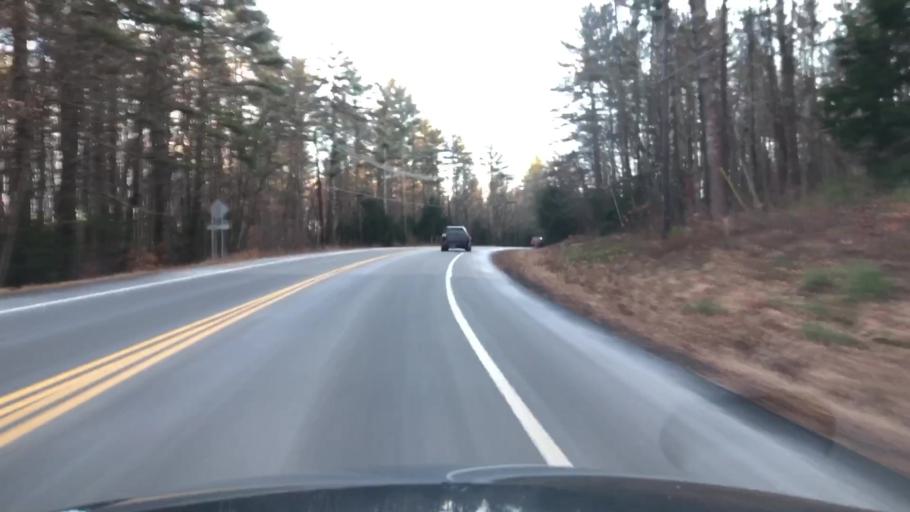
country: US
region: New Hampshire
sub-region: Hillsborough County
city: Brookline
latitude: 42.7473
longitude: -71.6677
